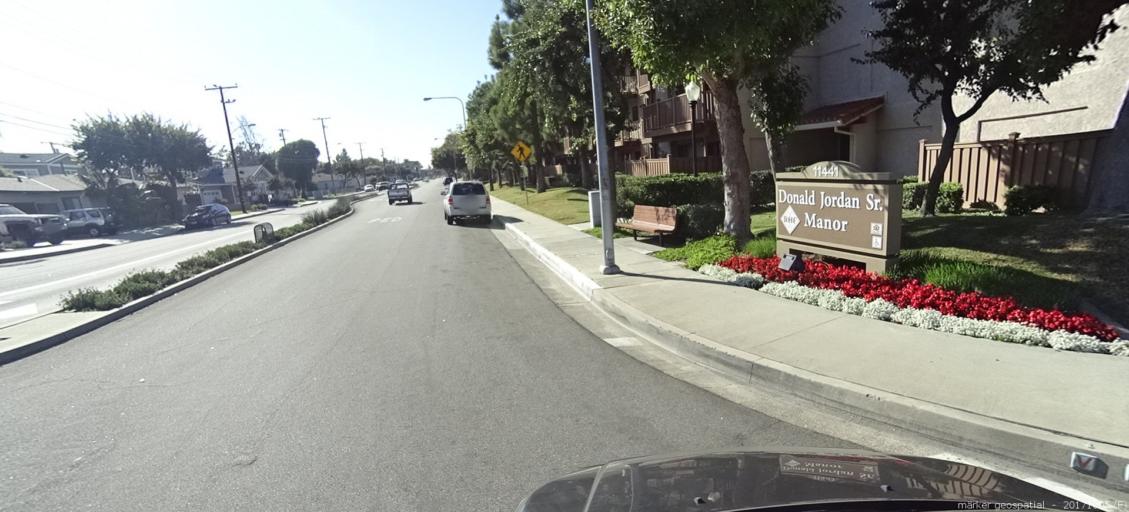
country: US
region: California
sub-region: Orange County
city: Garden Grove
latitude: 33.7761
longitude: -117.9323
